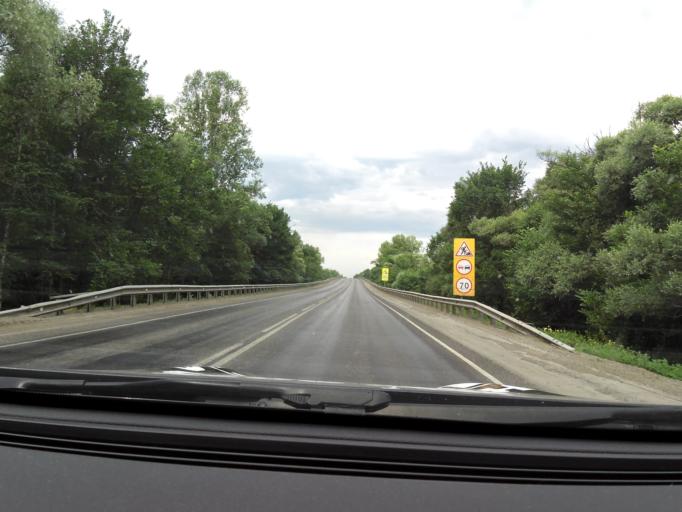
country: RU
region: Bashkortostan
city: Urman
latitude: 54.8274
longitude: 56.9097
